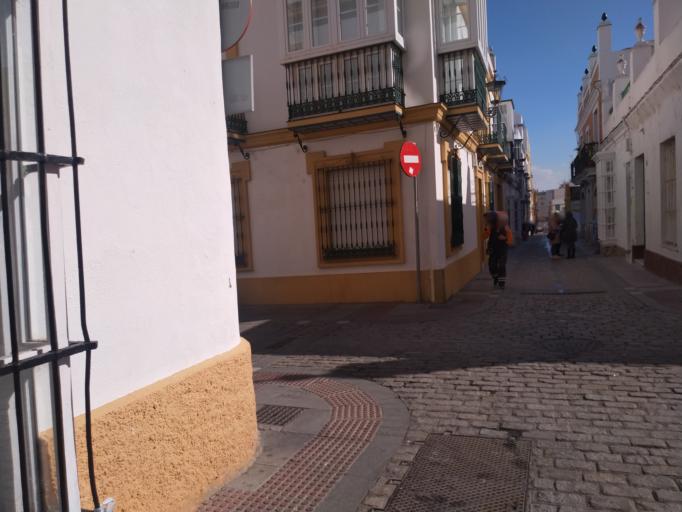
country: ES
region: Andalusia
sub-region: Provincia de Cadiz
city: San Fernando
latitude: 36.4643
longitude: -6.1968
